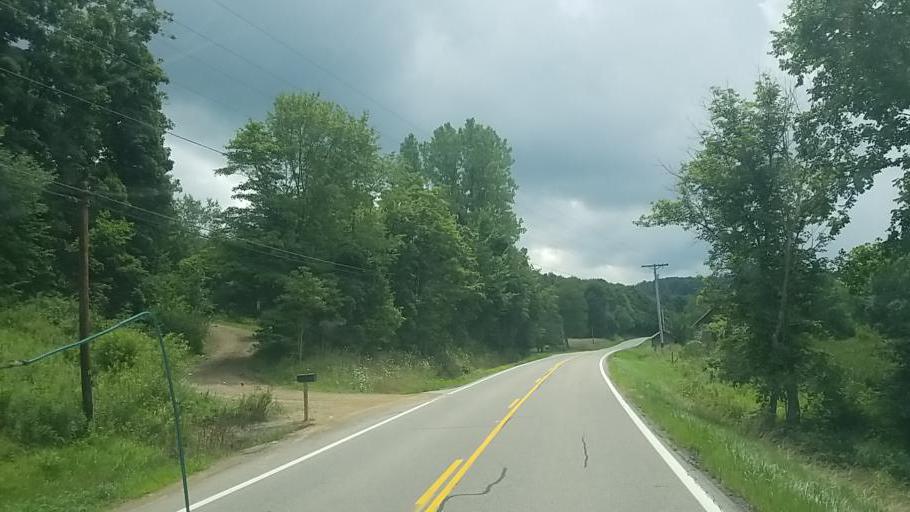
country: US
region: Ohio
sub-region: Muskingum County
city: Frazeysburg
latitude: 40.1829
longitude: -82.2646
